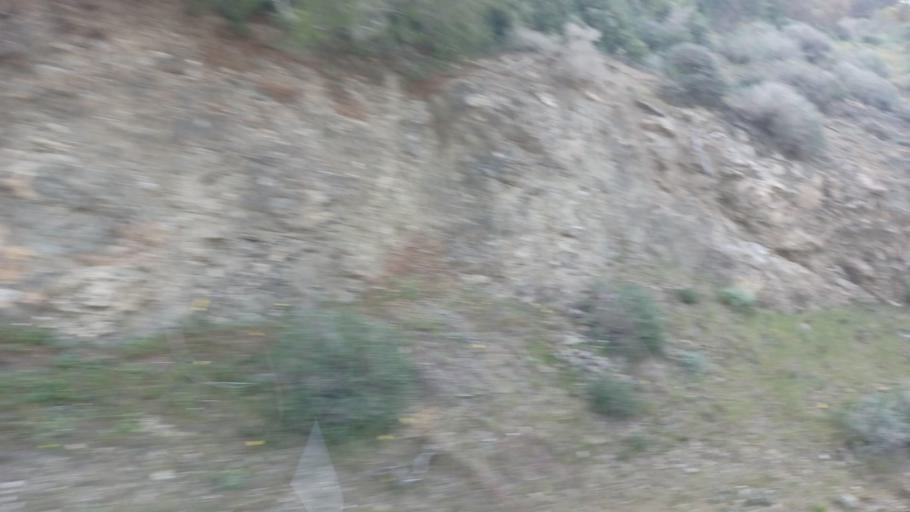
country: CY
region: Pafos
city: Polis
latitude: 35.0031
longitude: 32.3348
